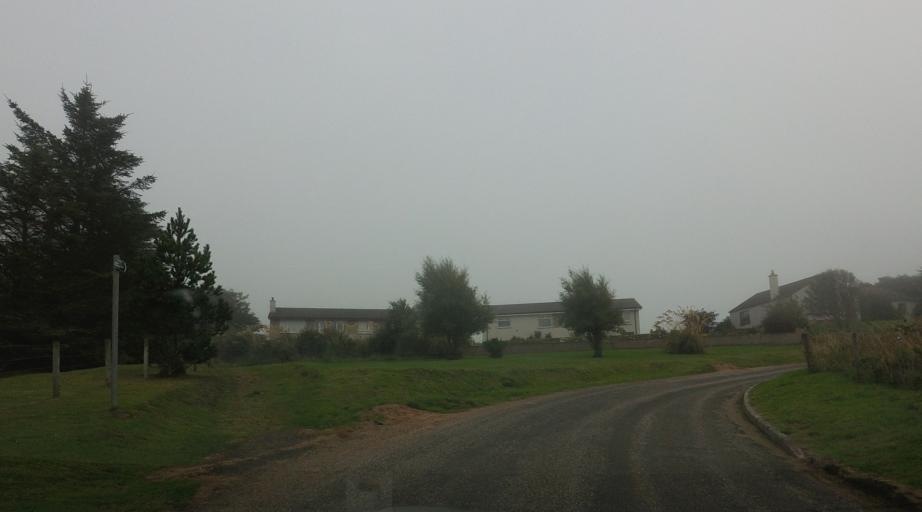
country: GB
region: Scotland
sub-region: Highland
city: Wick
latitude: 58.2999
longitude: -3.2884
